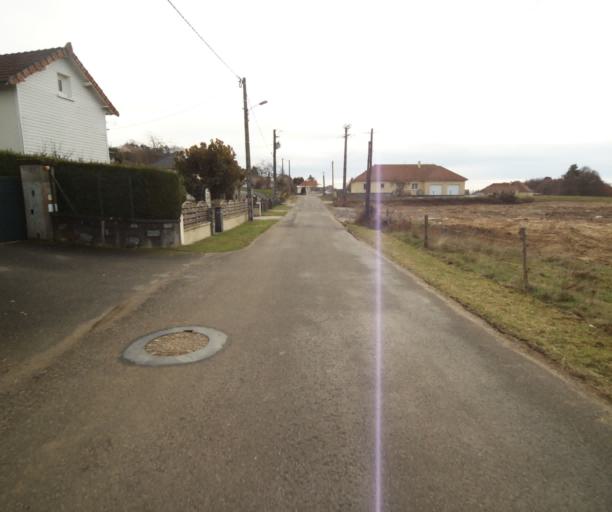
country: FR
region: Limousin
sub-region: Departement de la Correze
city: Saint-Mexant
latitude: 45.2703
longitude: 1.6797
